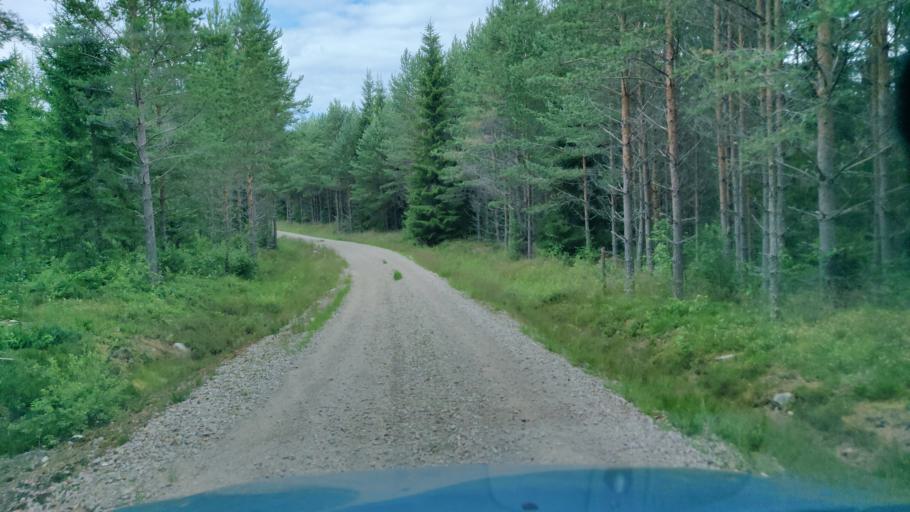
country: SE
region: Vaermland
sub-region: Hagfors Kommun
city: Hagfors
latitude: 59.9530
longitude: 13.5910
